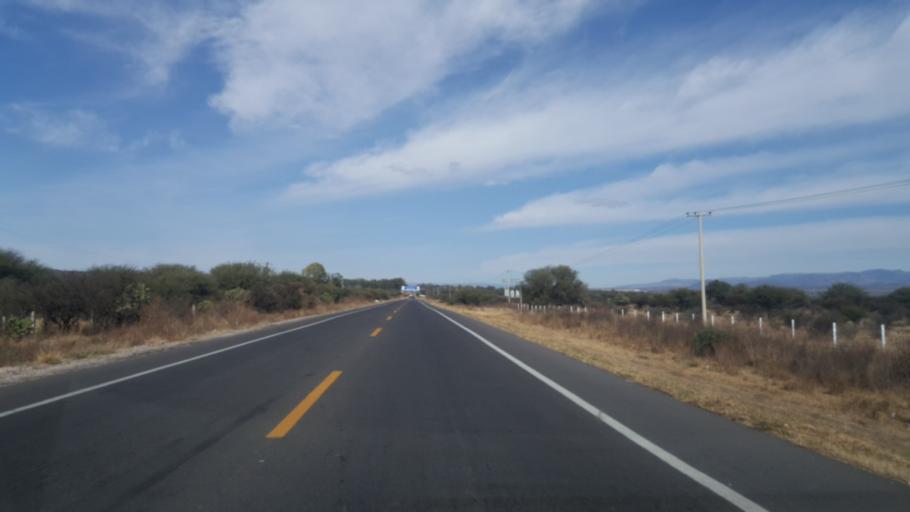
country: MX
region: Jalisco
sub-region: Lagos de Moreno
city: Cristeros [Fraccionamiento]
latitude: 21.2668
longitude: -101.9440
